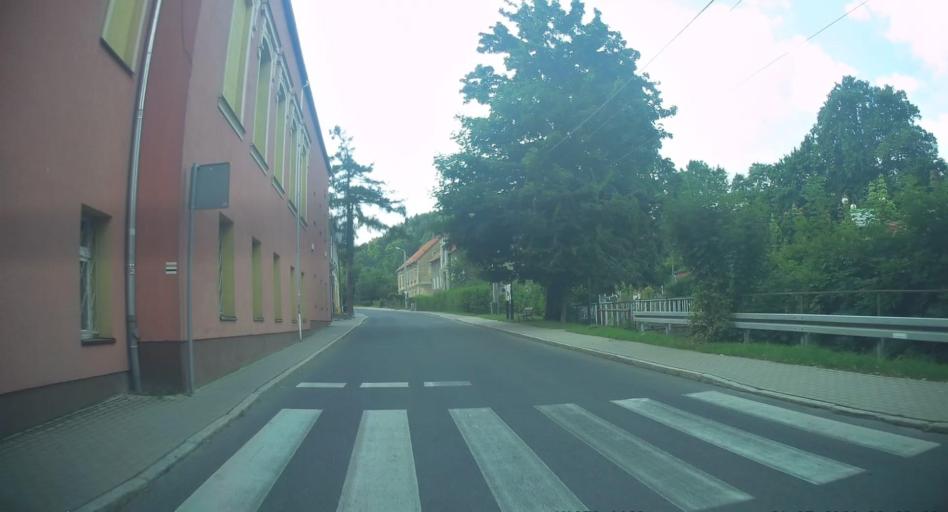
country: PL
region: Lower Silesian Voivodeship
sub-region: Powiat walbrzyski
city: Walim
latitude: 50.6973
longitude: 16.4422
